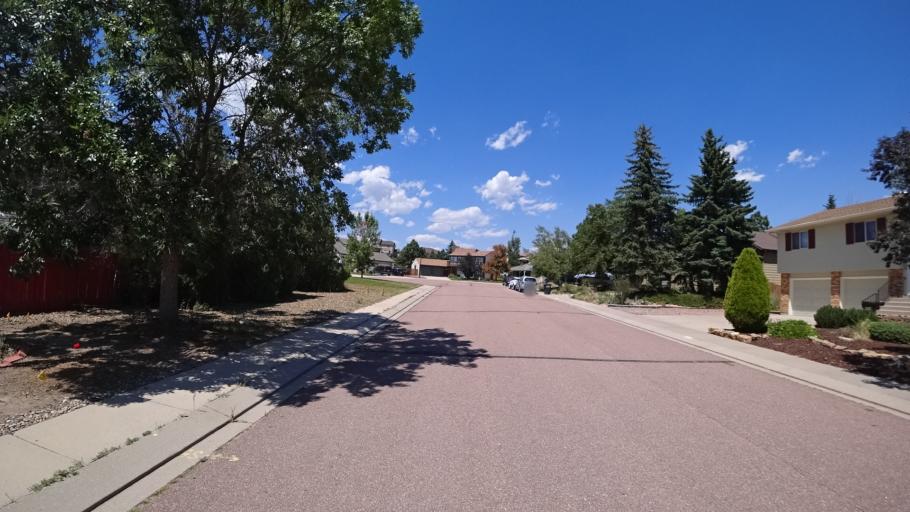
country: US
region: Colorado
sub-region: El Paso County
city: Black Forest
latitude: 38.9547
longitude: -104.7556
